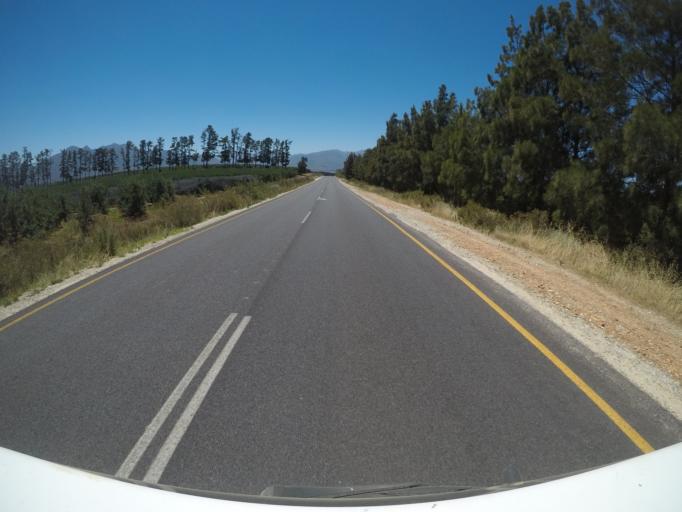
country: ZA
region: Western Cape
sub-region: Overberg District Municipality
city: Grabouw
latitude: -34.0656
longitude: 19.1328
